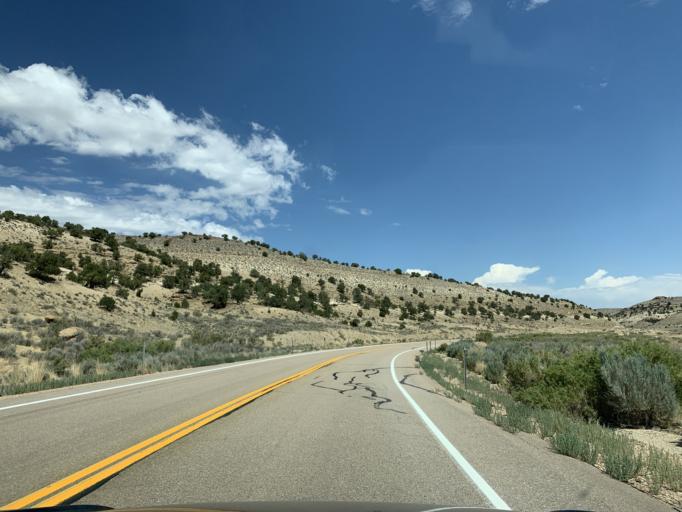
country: US
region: Utah
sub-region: Duchesne County
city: Duchesne
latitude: 39.9857
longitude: -110.1622
